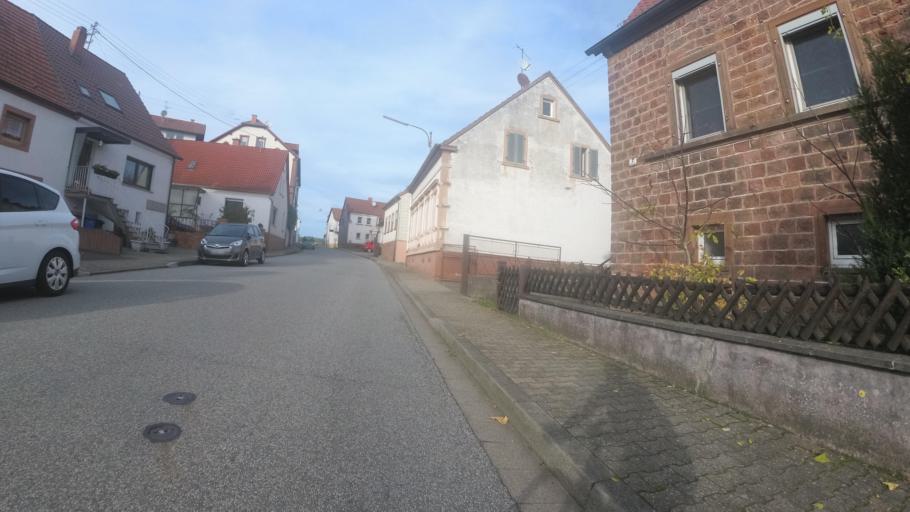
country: DE
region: Rheinland-Pfalz
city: Ramstein-Miesenbach
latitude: 49.4606
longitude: 7.5560
